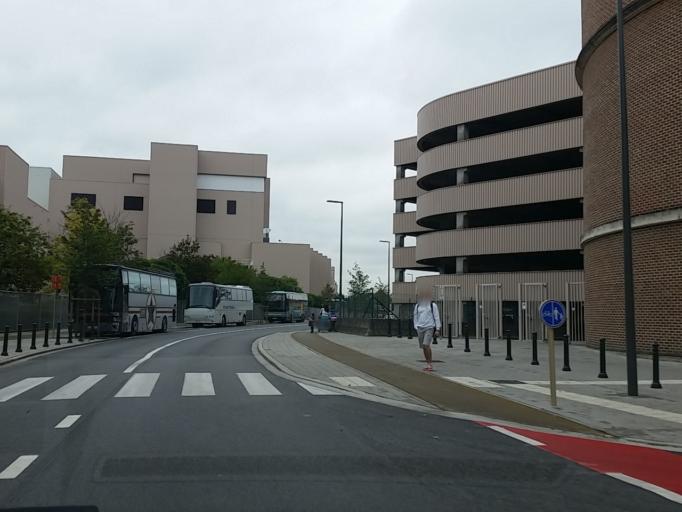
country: BE
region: Flanders
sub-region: Provincie Vlaams-Brabant
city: Drogenbos
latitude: 50.8121
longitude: 4.3158
